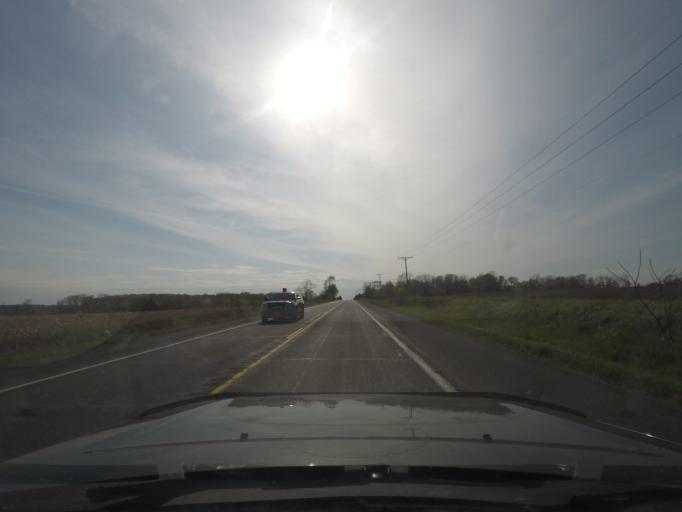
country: US
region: Michigan
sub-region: Berrien County
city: Three Oaks
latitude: 41.7985
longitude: -86.5673
